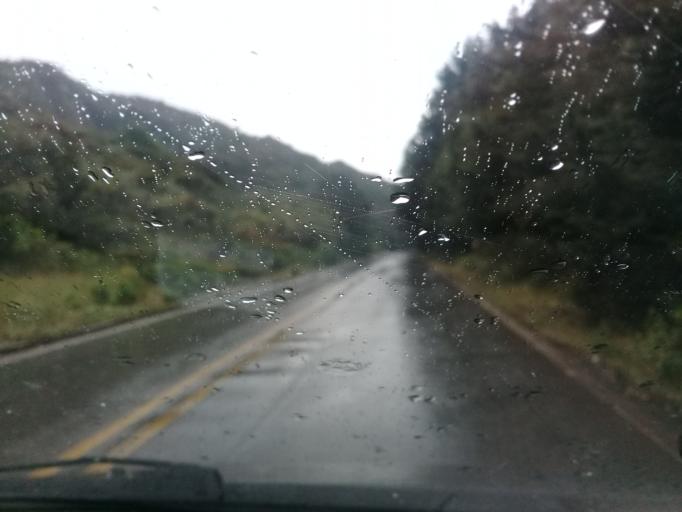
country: CO
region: Cundinamarca
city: Guasca
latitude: 4.8466
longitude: -73.8219
